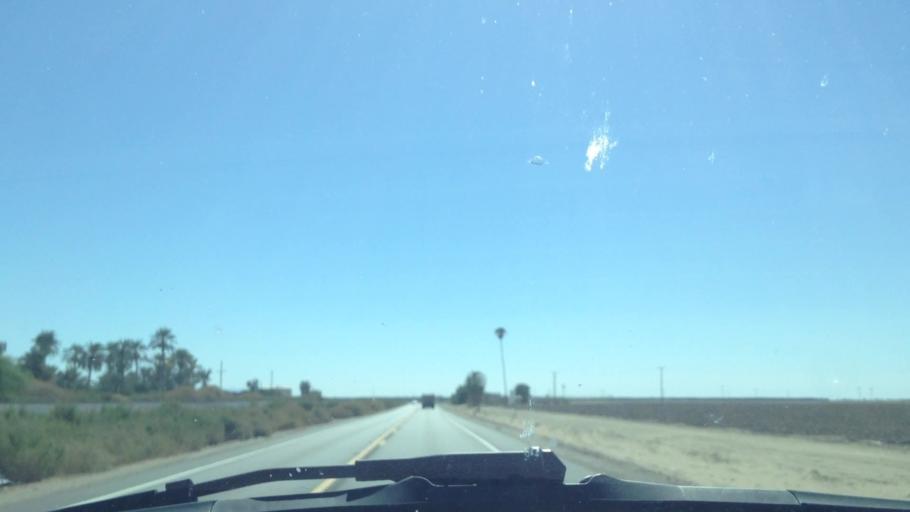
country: US
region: California
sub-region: Riverside County
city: Mecca
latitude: 33.5418
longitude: -116.0336
